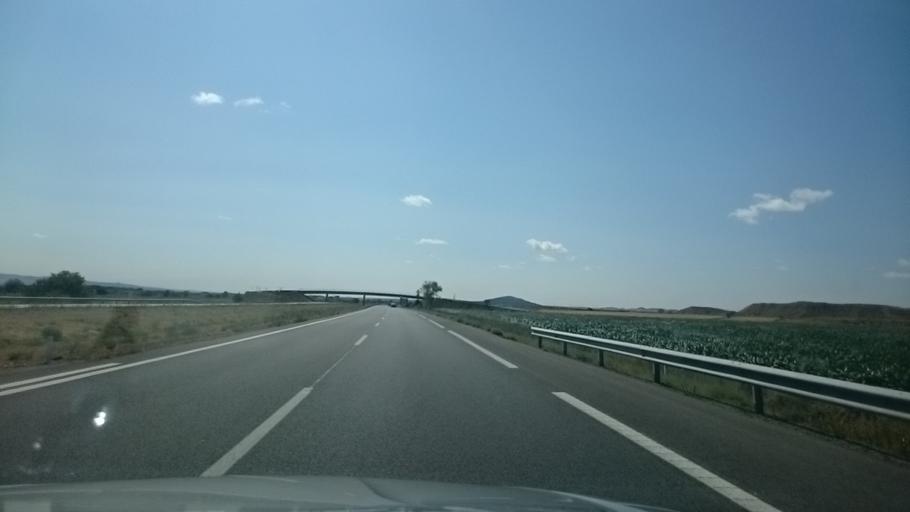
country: ES
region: Aragon
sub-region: Provincia de Zaragoza
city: Frescano
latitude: 41.9264
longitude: -1.4916
